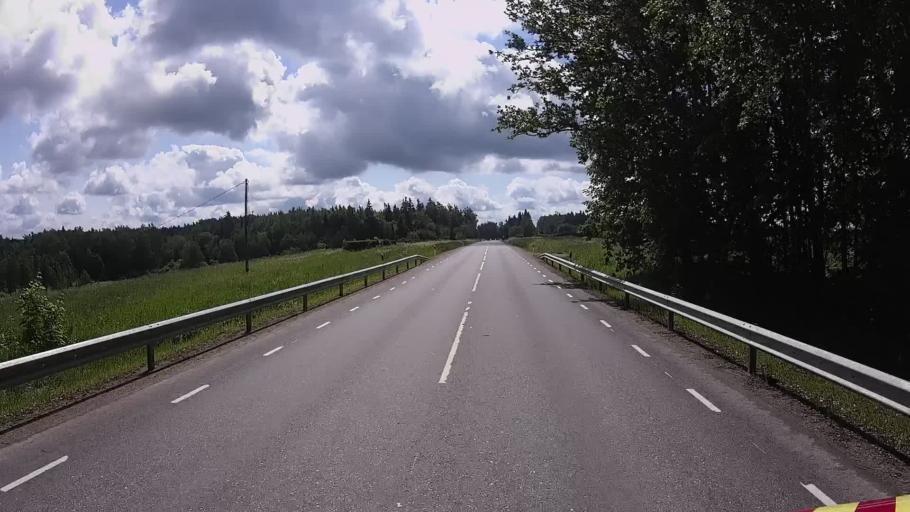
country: EE
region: Viljandimaa
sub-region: Viiratsi vald
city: Viiratsi
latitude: 58.3246
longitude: 25.6596
